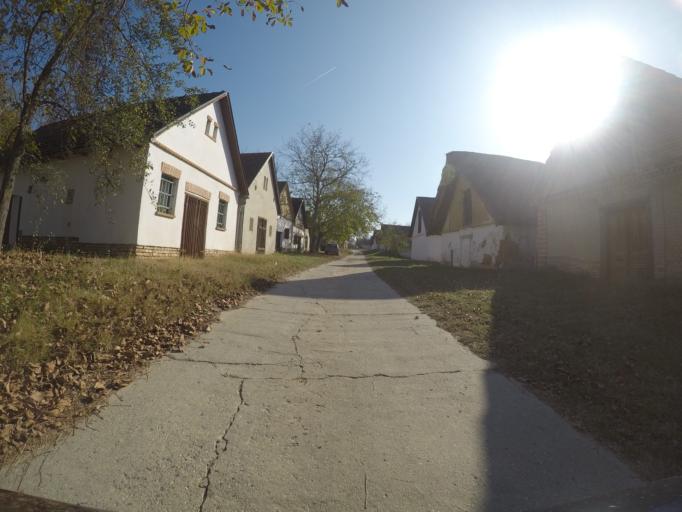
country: HU
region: Tolna
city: Nagydorog
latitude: 46.6345
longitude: 18.7053
